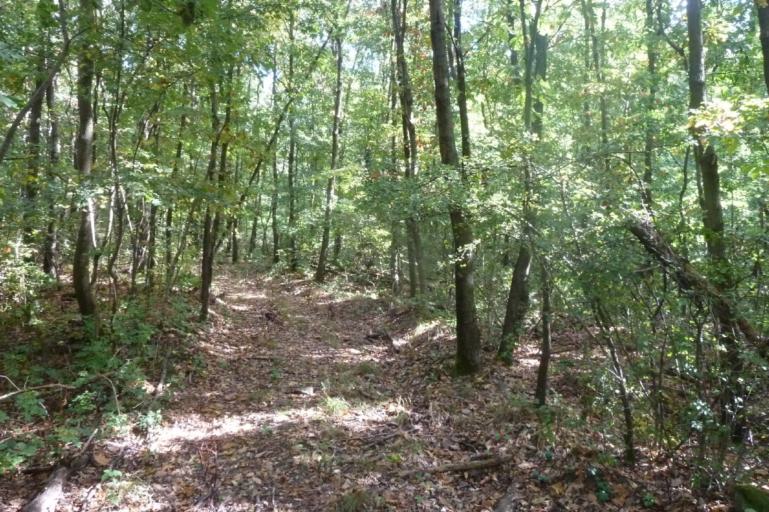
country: HU
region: Pest
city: Csobanka
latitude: 47.6876
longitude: 18.9577
